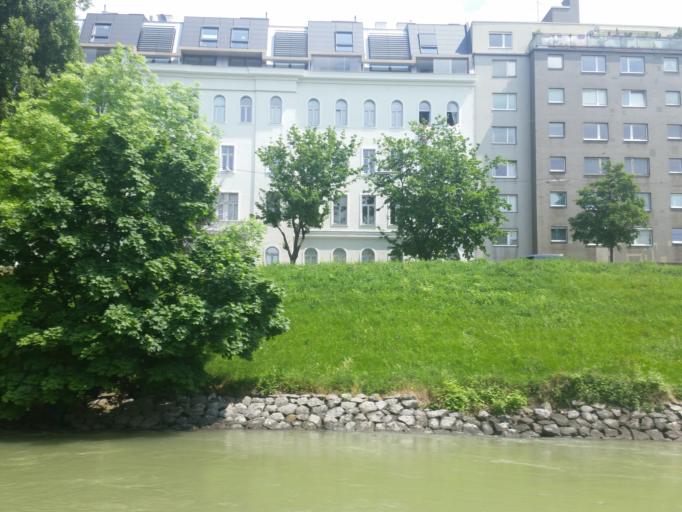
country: AT
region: Vienna
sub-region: Wien Stadt
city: Vienna
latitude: 48.2103
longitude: 16.3960
